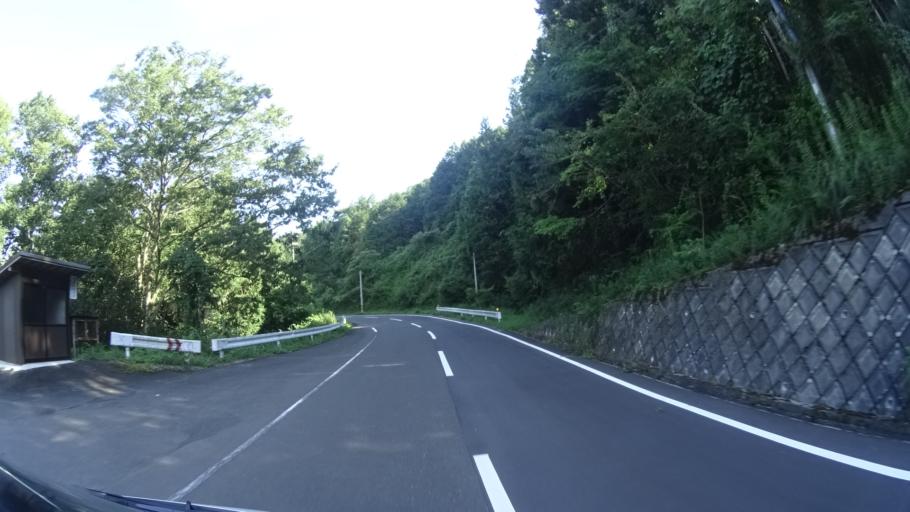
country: JP
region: Kyoto
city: Ayabe
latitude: 35.2771
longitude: 135.3309
